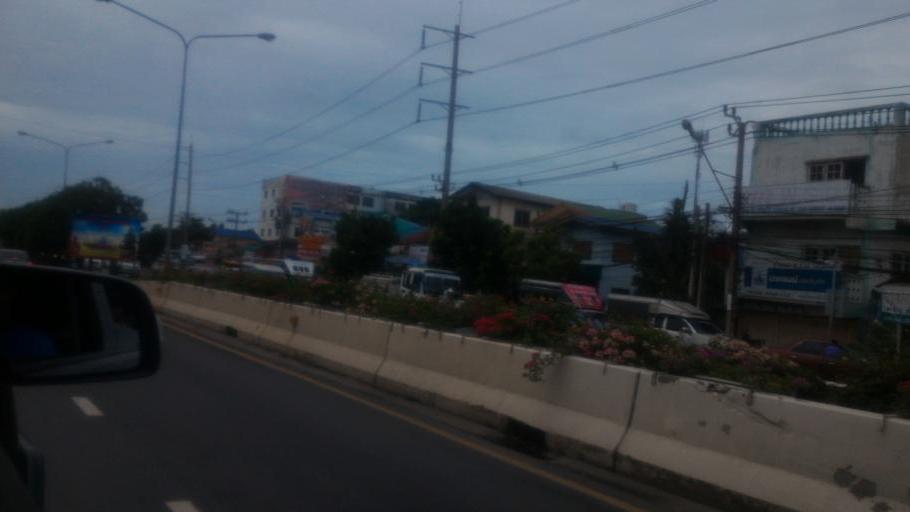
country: TH
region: Bangkok
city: Bang Khun Thian
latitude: 13.6211
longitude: 100.4380
